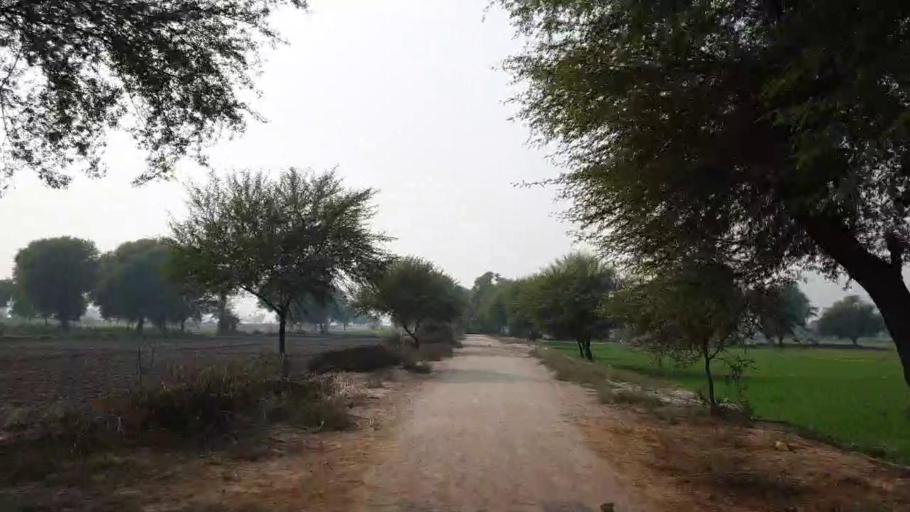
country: PK
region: Sindh
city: Bhan
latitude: 26.5315
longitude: 67.7116
